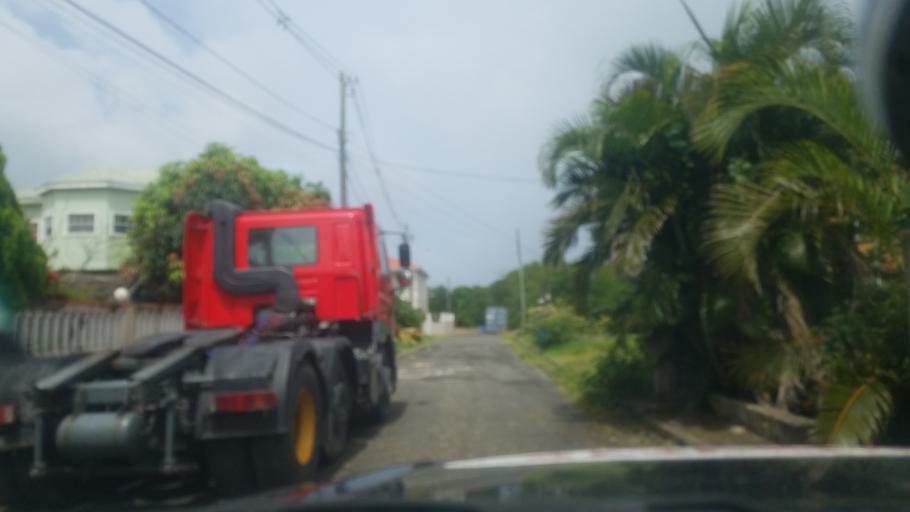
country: LC
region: Laborie Quarter
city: Laborie
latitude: 13.7480
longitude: -60.9747
